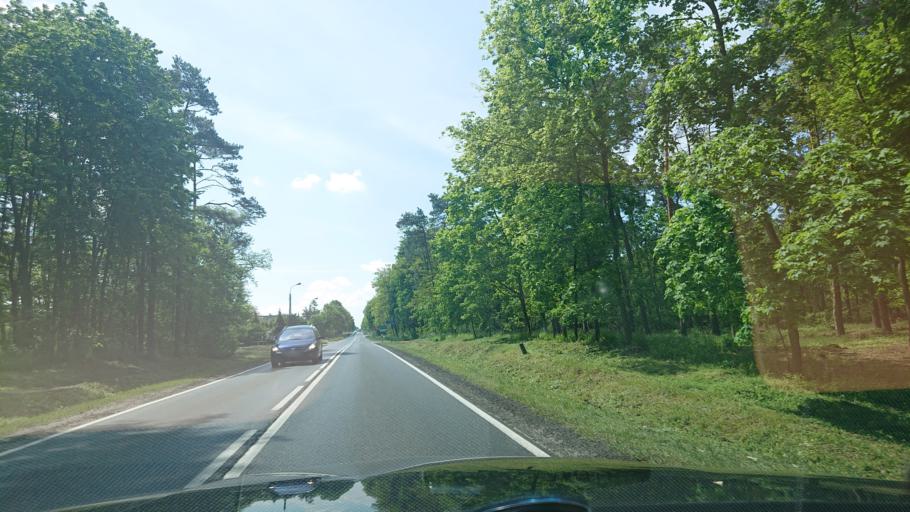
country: PL
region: Greater Poland Voivodeship
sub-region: Powiat gnieznienski
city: Gniezno
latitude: 52.4848
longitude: 17.5935
